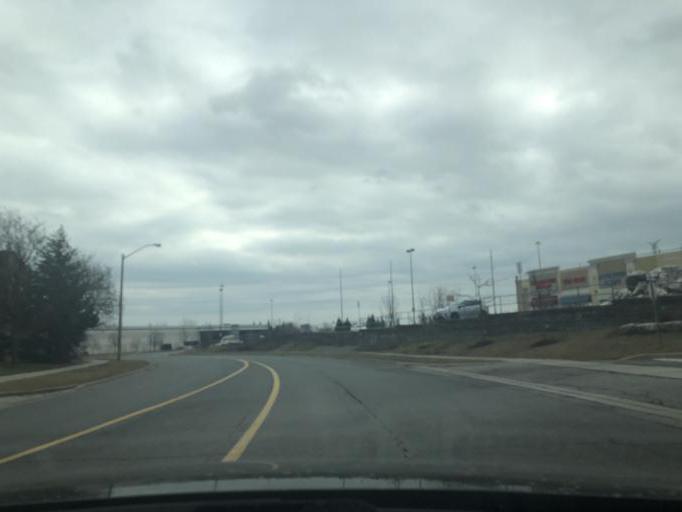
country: CA
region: Ontario
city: Scarborough
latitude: 43.7995
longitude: -79.1967
